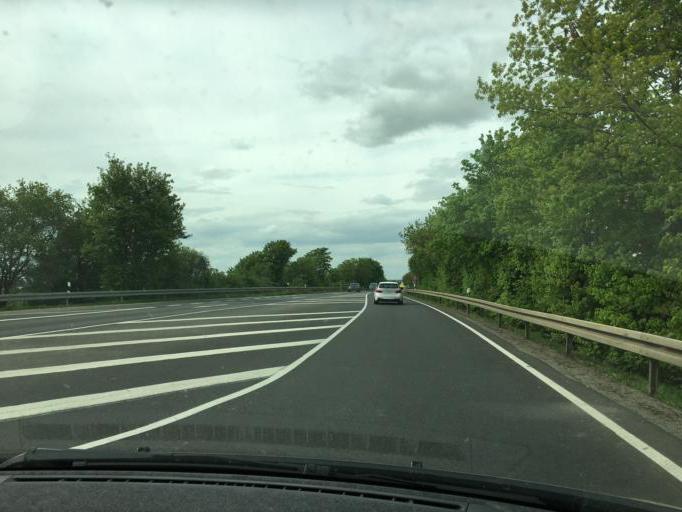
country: DE
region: North Rhine-Westphalia
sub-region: Regierungsbezirk Koln
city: Euskirchen
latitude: 50.6831
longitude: 6.7499
